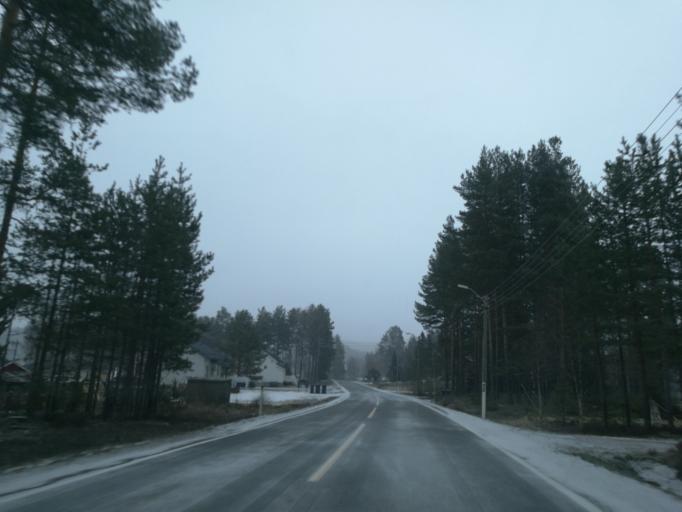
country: NO
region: Hedmark
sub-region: Asnes
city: Flisa
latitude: 60.7042
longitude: 12.3508
